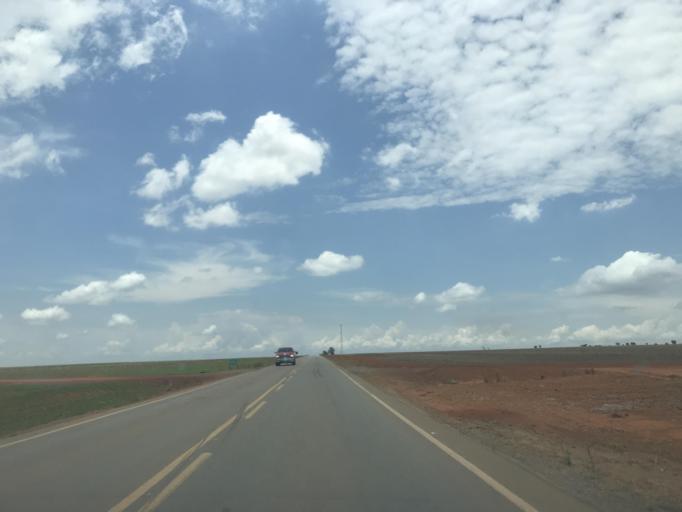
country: BR
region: Goias
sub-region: Vianopolis
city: Vianopolis
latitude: -16.5276
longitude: -48.2417
